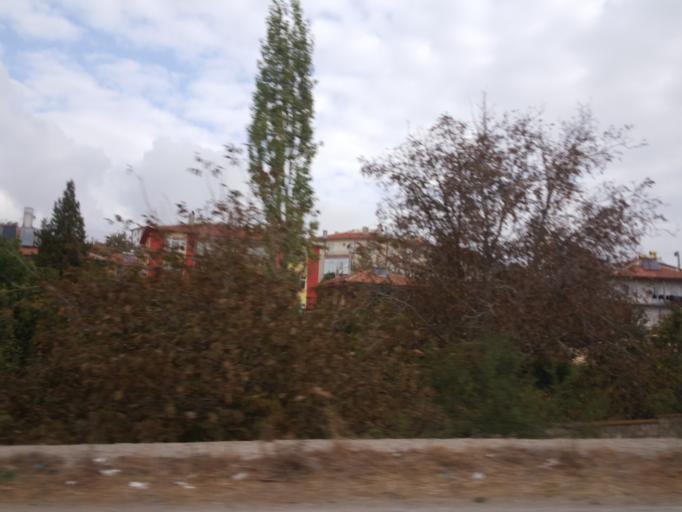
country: TR
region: Kirikkale
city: Keskin
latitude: 39.6724
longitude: 33.6079
